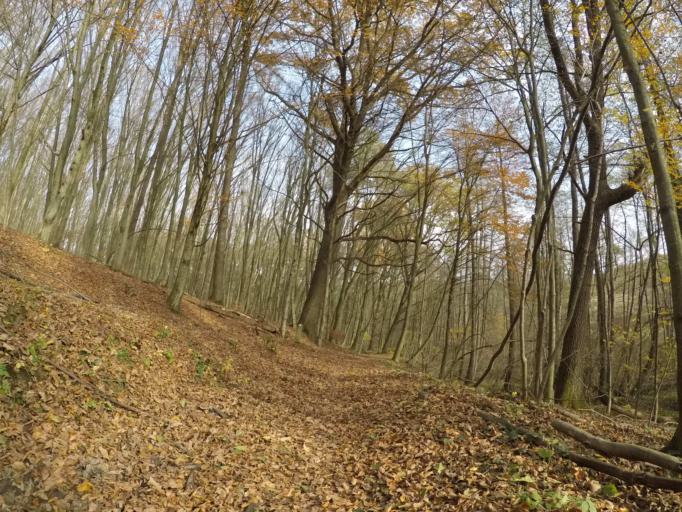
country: SK
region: Presovsky
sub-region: Okres Presov
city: Presov
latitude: 48.9573
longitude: 21.1923
